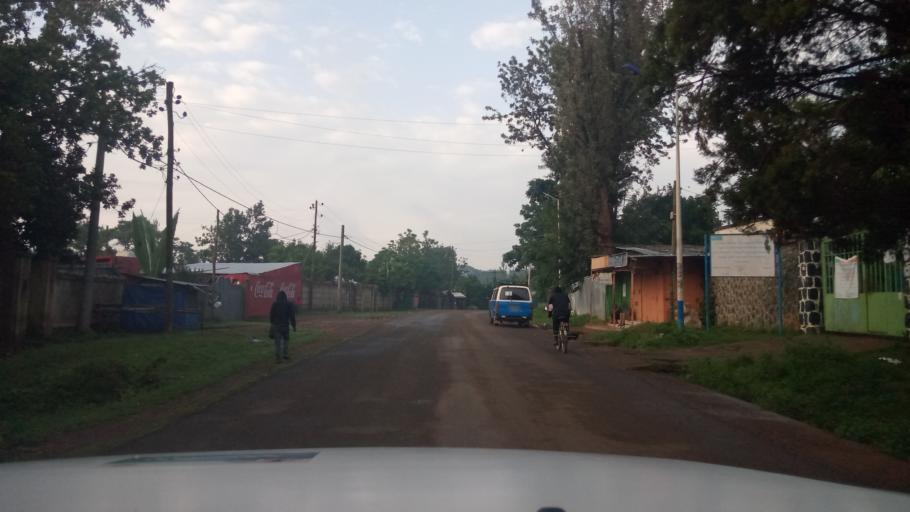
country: ET
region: Oromiya
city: Jima
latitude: 7.6777
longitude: 36.8401
